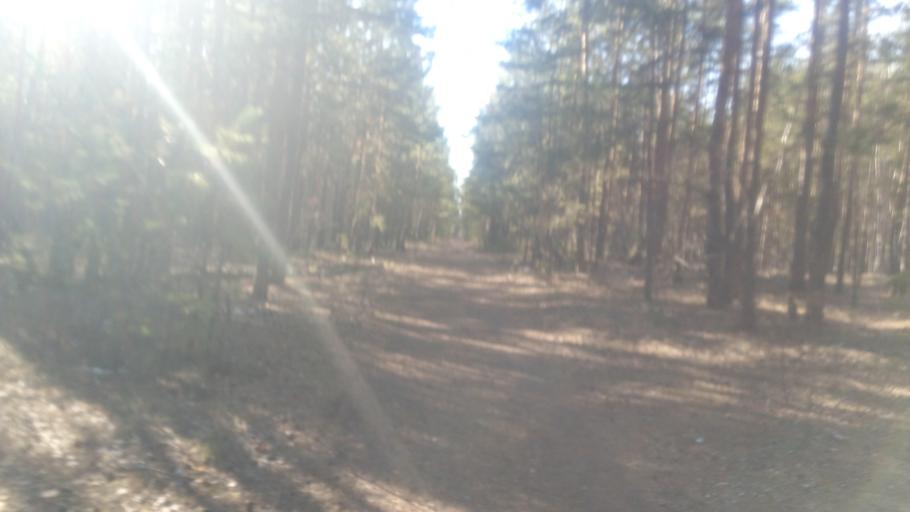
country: RU
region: Chelyabinsk
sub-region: Gorod Chelyabinsk
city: Chelyabinsk
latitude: 55.1589
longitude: 61.3397
